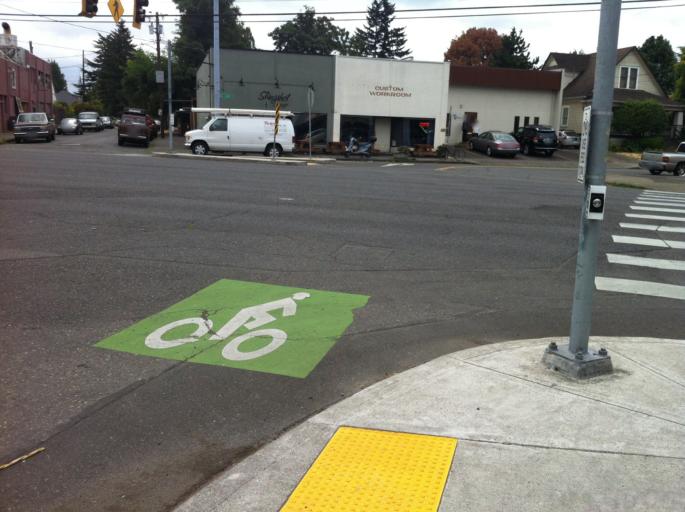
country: US
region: Oregon
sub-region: Multnomah County
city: Lents
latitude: 45.4942
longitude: -122.6055
